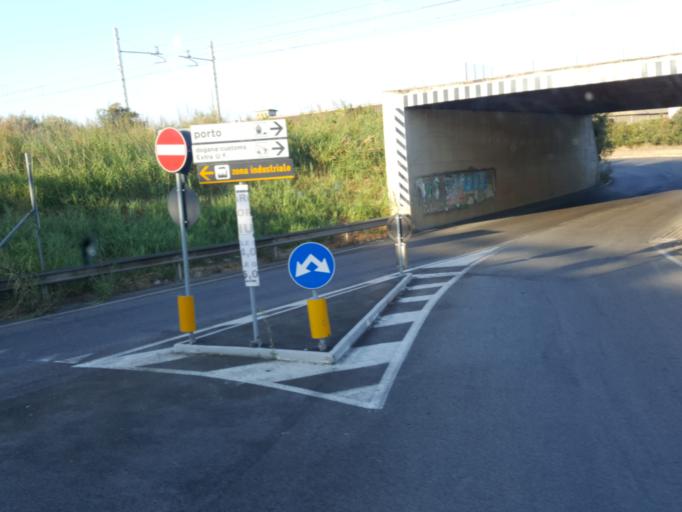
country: IT
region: Latium
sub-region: Citta metropolitana di Roma Capitale
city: Aurelia
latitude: 42.1192
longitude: 11.7710
